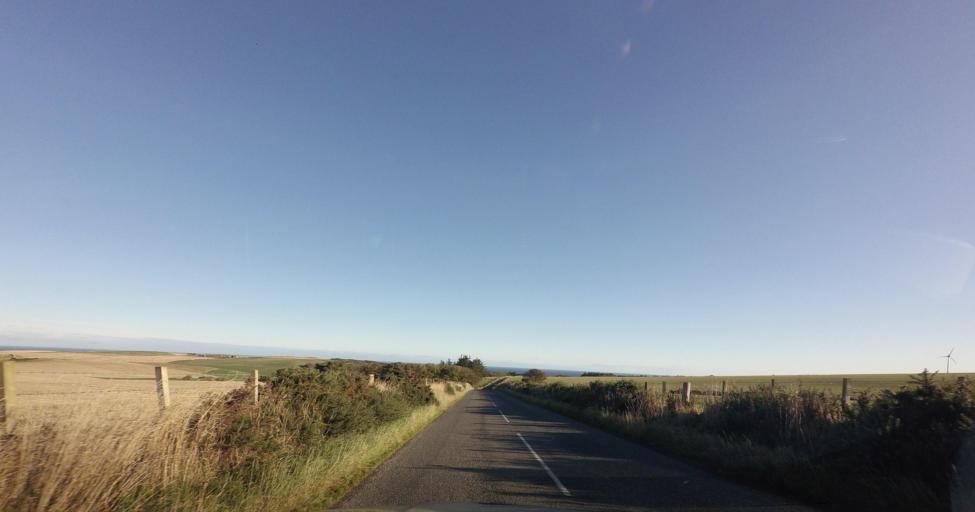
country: GB
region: Scotland
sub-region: Aberdeenshire
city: Rosehearty
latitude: 57.6713
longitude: -2.3014
